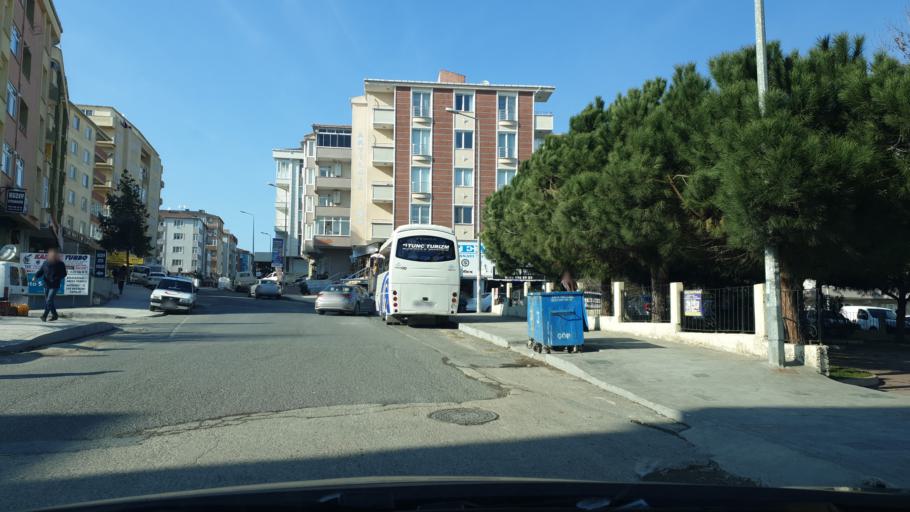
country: TR
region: Tekirdag
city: Cerkezkoey
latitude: 41.2830
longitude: 27.9955
